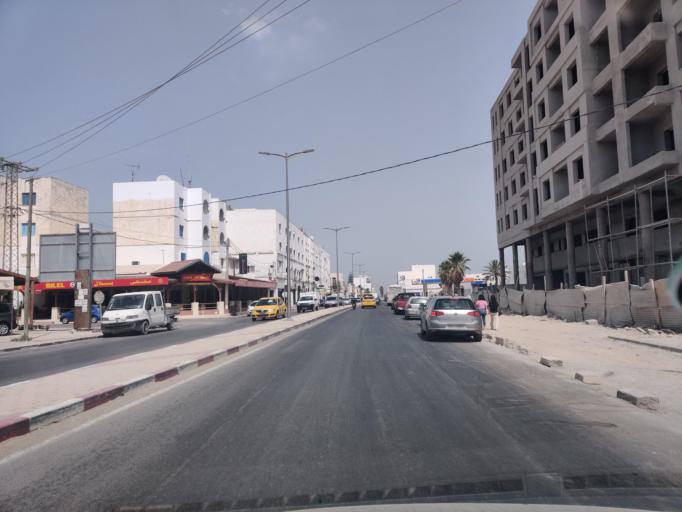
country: TN
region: Nabul
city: Bu `Urqub
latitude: 36.5942
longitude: 10.5020
